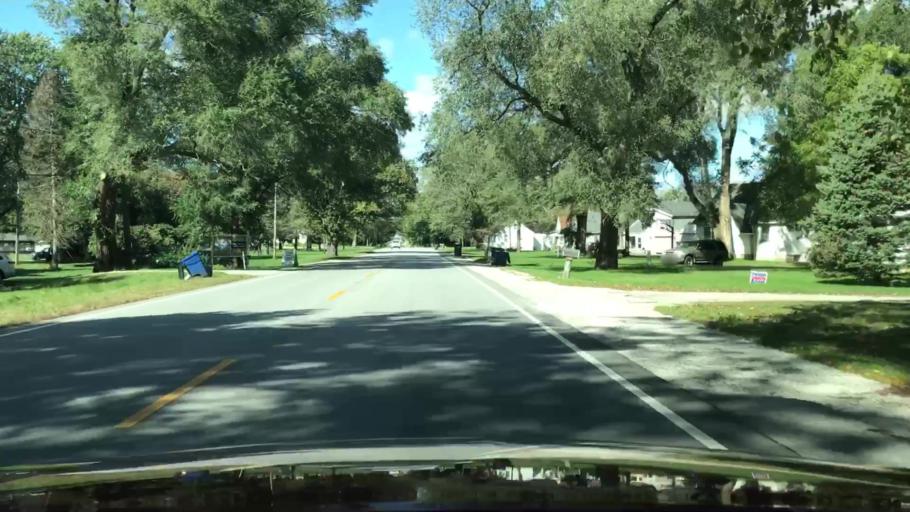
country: US
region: Illinois
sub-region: Cook County
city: Lynwood
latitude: 41.5199
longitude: -87.5495
